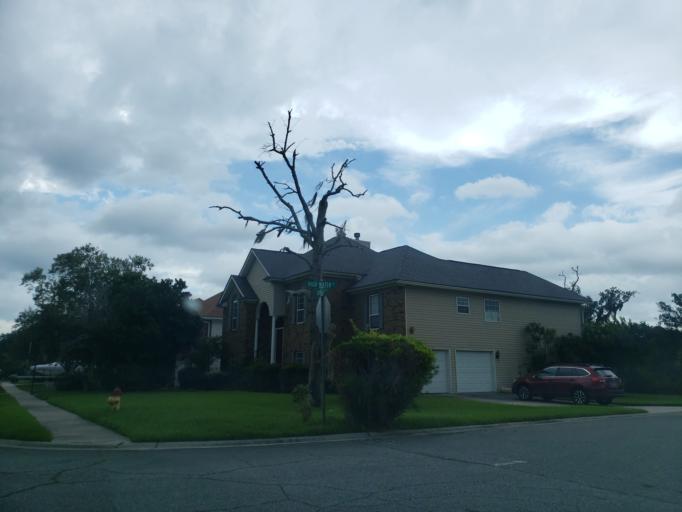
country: US
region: Georgia
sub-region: Chatham County
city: Wilmington Island
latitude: 32.0233
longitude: -80.9546
